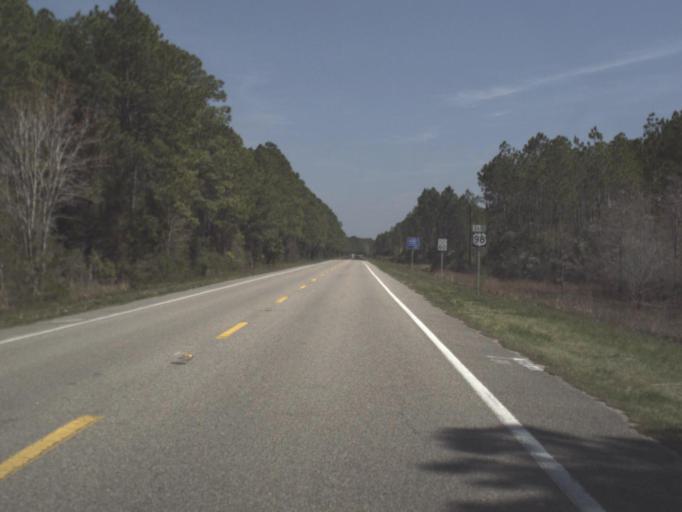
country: US
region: Florida
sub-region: Gulf County
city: Port Saint Joe
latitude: 29.7366
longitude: -85.1687
